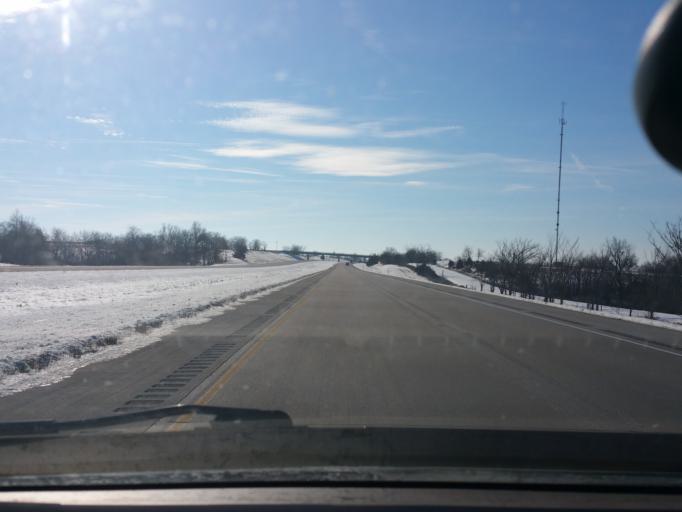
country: US
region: Iowa
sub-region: Decatur County
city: Leon
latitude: 40.7636
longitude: -93.8367
